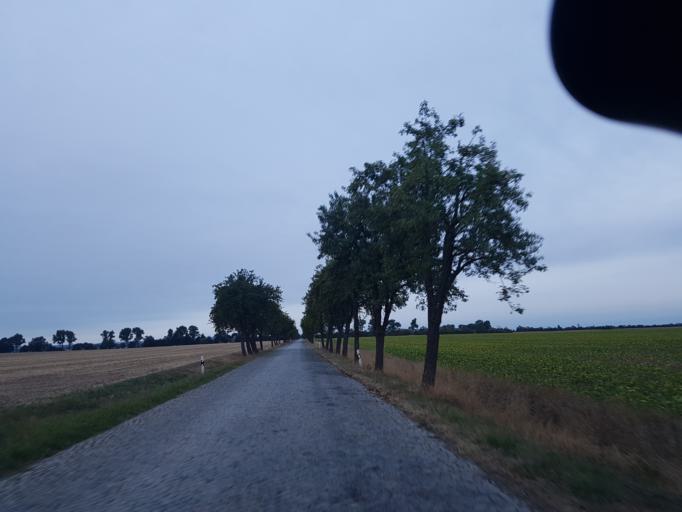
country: DE
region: Brandenburg
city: Muhlberg
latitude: 51.4964
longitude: 13.2220
